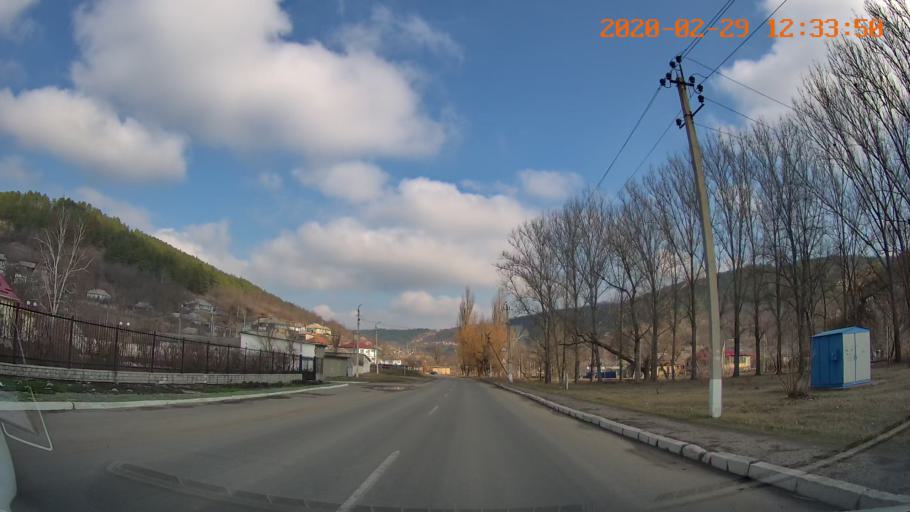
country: MD
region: Telenesti
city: Camenca
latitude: 48.0375
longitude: 28.7081
